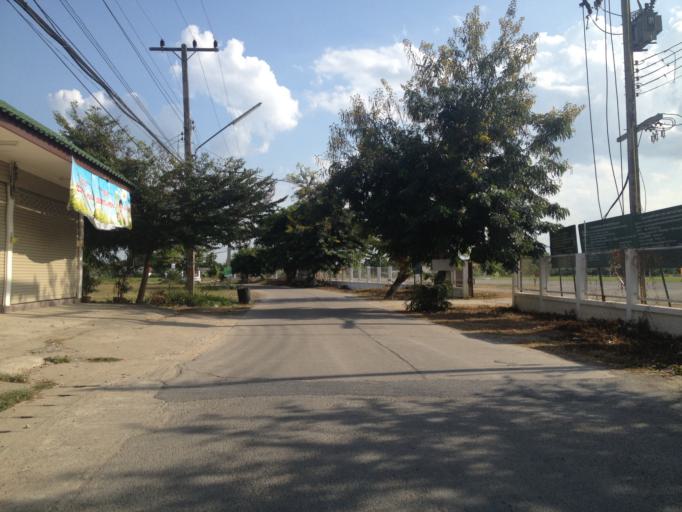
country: TH
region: Chiang Mai
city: Hang Dong
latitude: 18.7054
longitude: 98.9233
